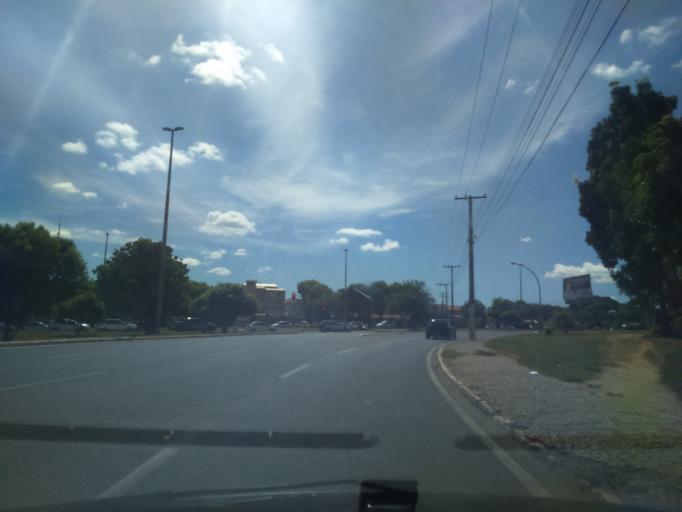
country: BR
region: Federal District
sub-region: Brasilia
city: Brasilia
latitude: -15.8473
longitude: -47.9750
